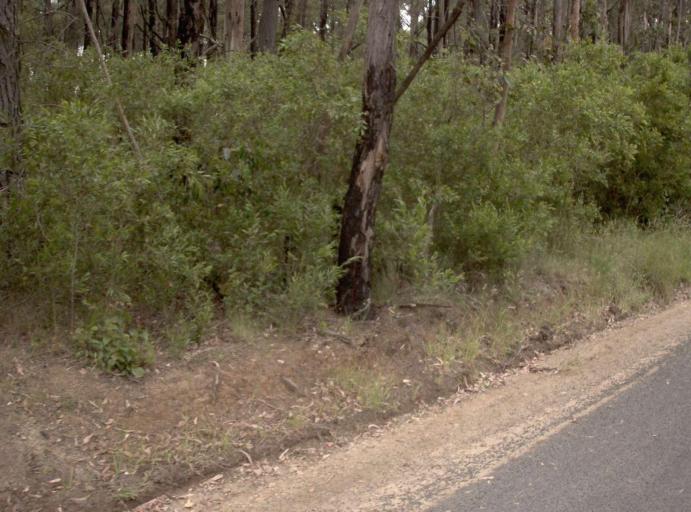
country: AU
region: Victoria
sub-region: Latrobe
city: Moe
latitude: -38.3123
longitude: 146.2675
